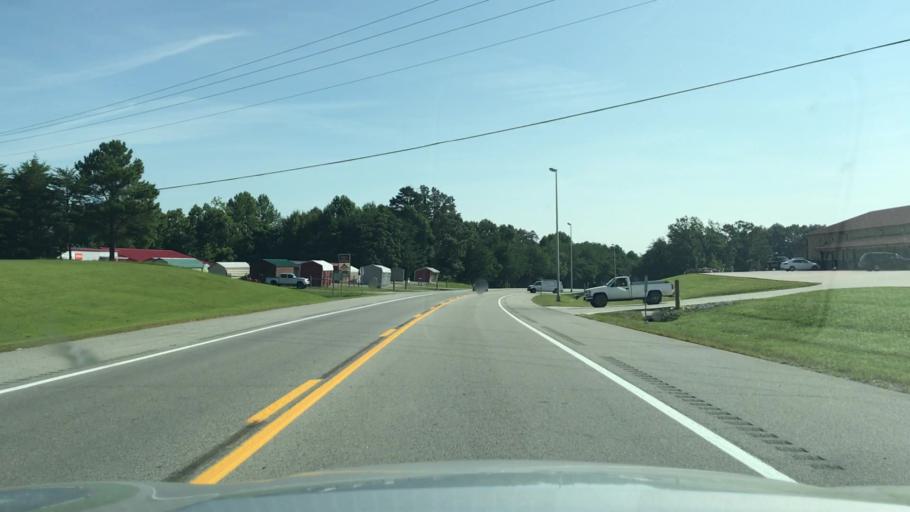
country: US
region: Tennessee
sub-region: Pickett County
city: Byrdstown
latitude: 36.5808
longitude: -85.1347
